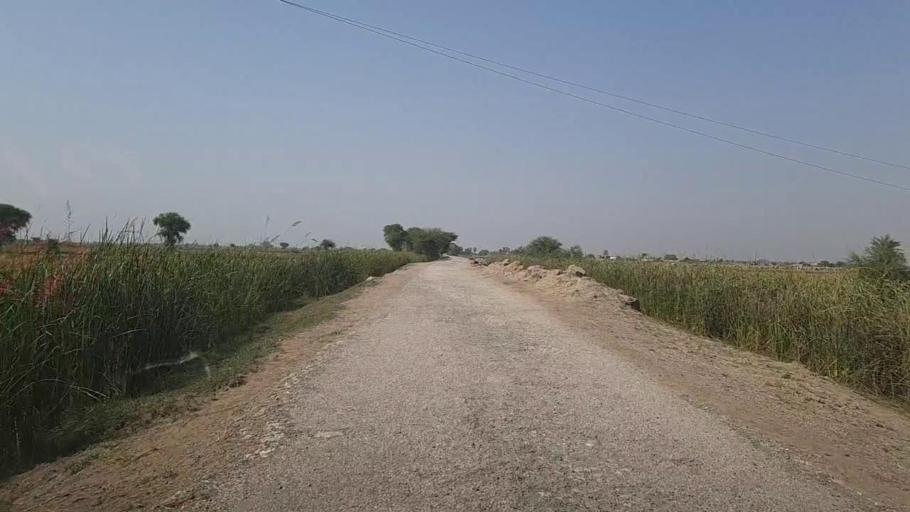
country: PK
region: Sindh
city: Kandhkot
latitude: 28.4008
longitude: 69.2635
